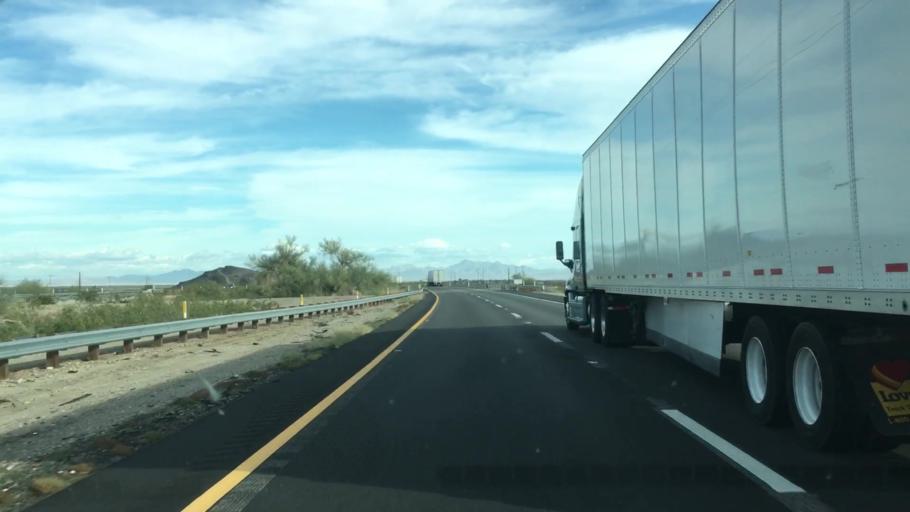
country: US
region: California
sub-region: Riverside County
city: Mesa Verde
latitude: 33.6087
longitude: -114.7712
